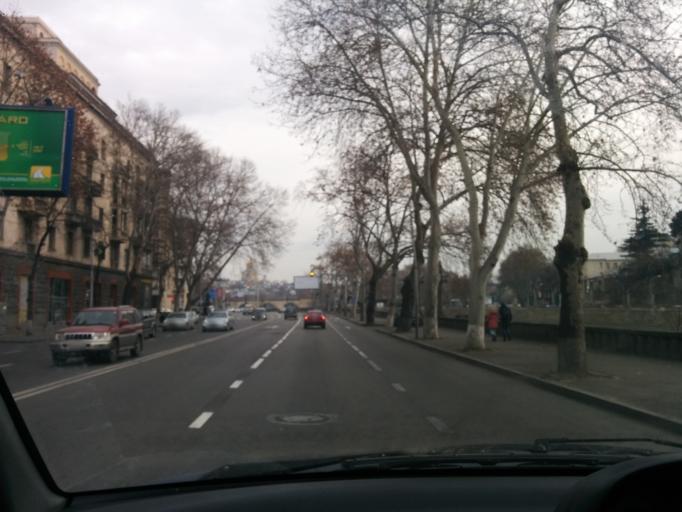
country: GE
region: T'bilisi
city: Tbilisi
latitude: 41.7046
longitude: 44.7973
